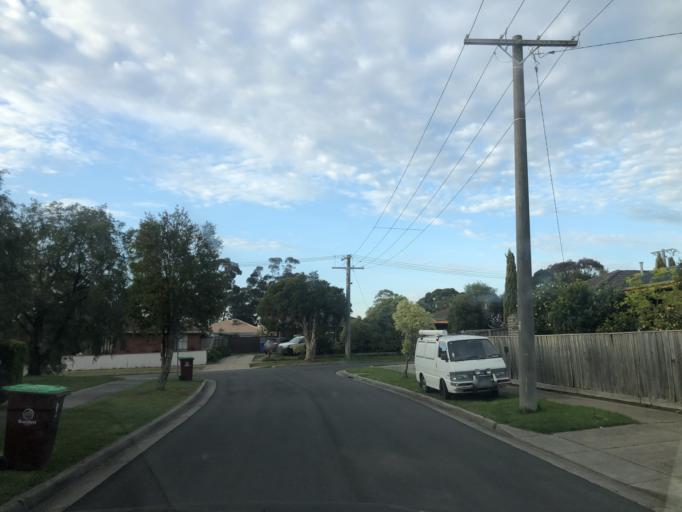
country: AU
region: Victoria
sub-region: Casey
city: Hampton Park
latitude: -38.0329
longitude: 145.2524
